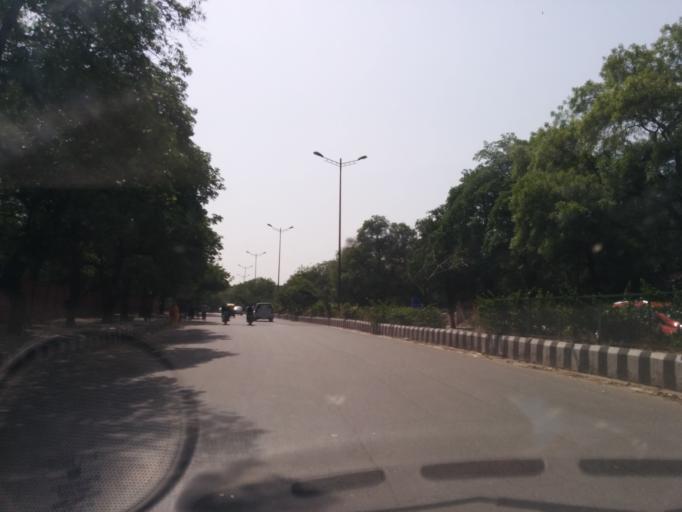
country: IN
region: NCT
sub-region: New Delhi
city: New Delhi
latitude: 28.5317
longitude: 77.1953
